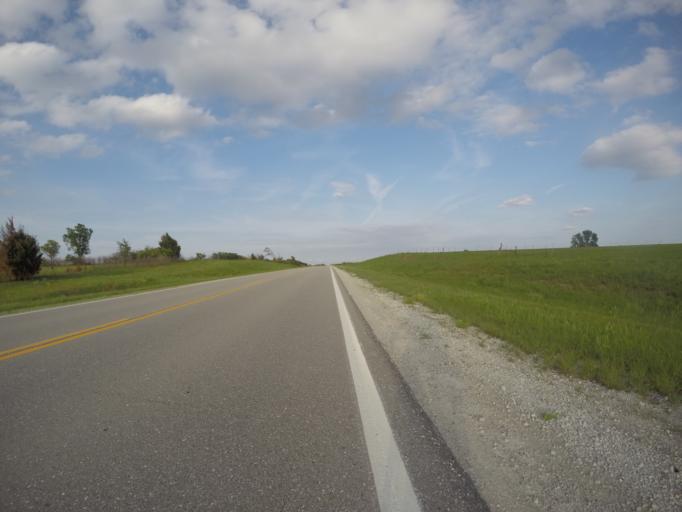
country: US
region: Kansas
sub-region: Pottawatomie County
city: Westmoreland
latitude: 39.4283
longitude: -96.5740
